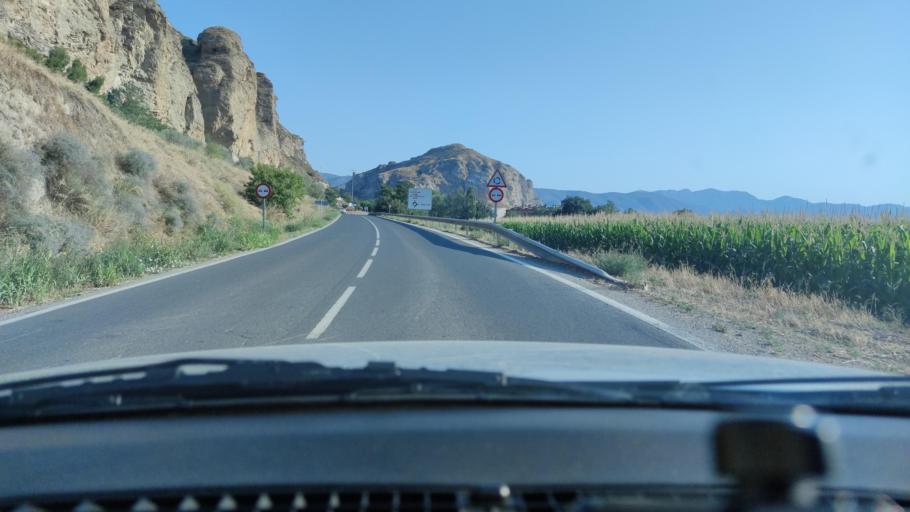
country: ES
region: Catalonia
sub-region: Provincia de Lleida
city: Balaguer
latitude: 41.8180
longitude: 0.8041
